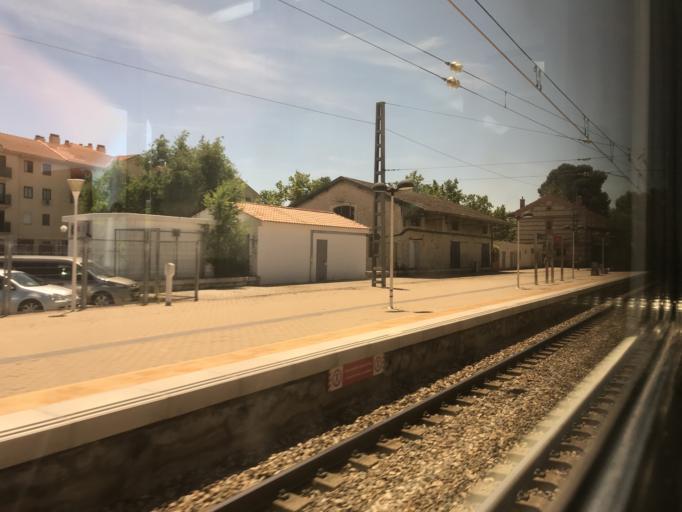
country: ES
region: Madrid
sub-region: Provincia de Madrid
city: Pinto
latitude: 40.2440
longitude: -3.7038
